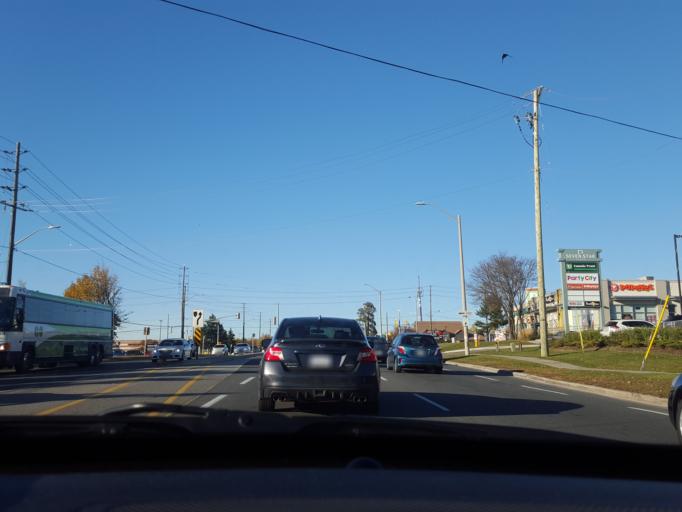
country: CA
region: Ontario
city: Markham
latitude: 43.8660
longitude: -79.2842
